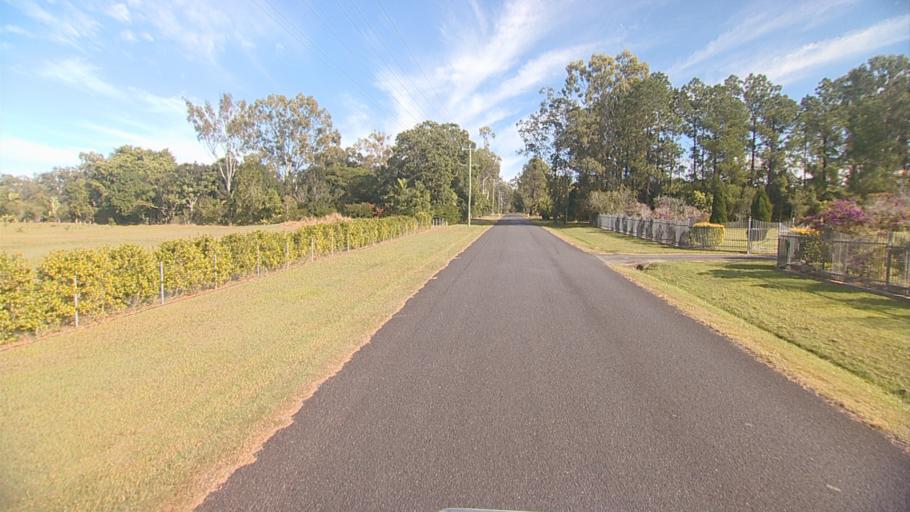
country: AU
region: Queensland
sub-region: Brisbane
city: Forest Lake
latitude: -27.6577
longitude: 152.9858
